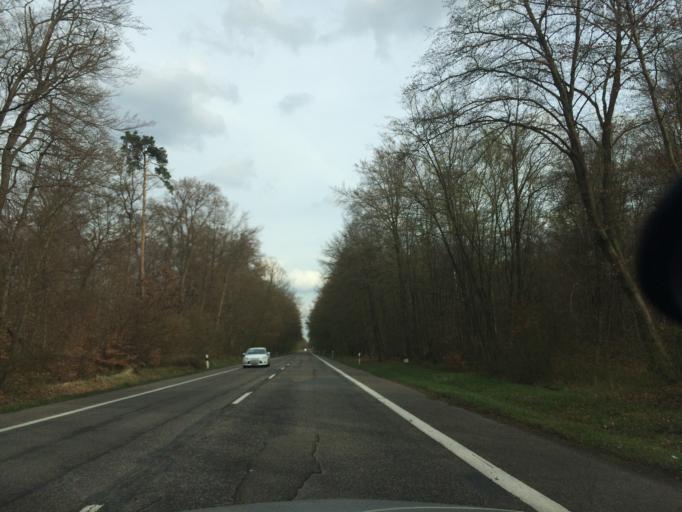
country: DE
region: Hesse
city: Langen
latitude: 50.0283
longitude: 8.6325
